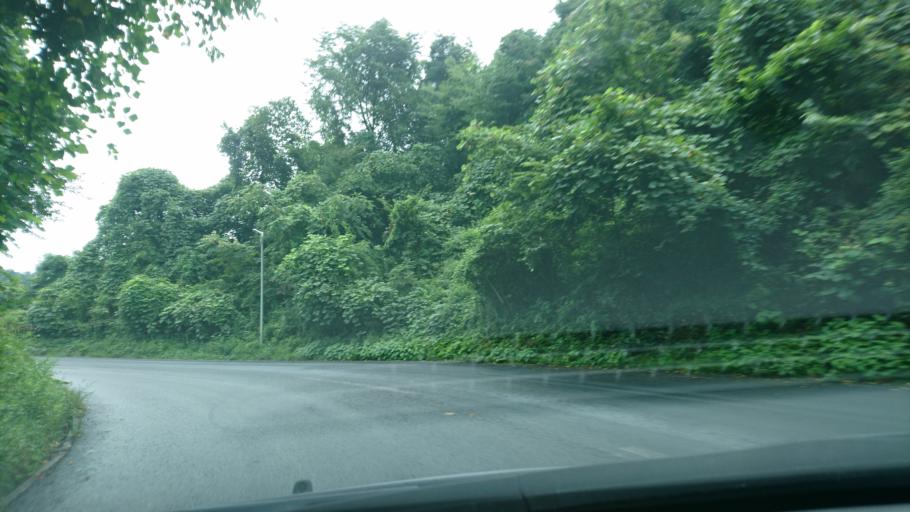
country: JP
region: Iwate
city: Ichinoseki
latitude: 38.9376
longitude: 141.1831
